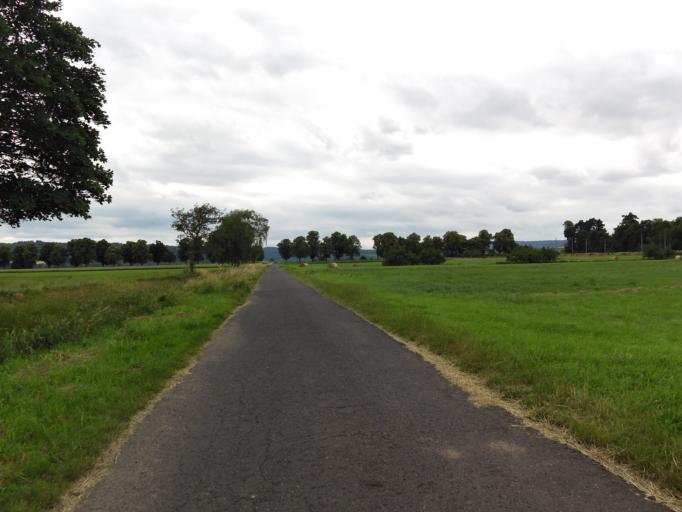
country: DE
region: Thuringia
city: Lauchroden
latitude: 51.0019
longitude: 10.1653
